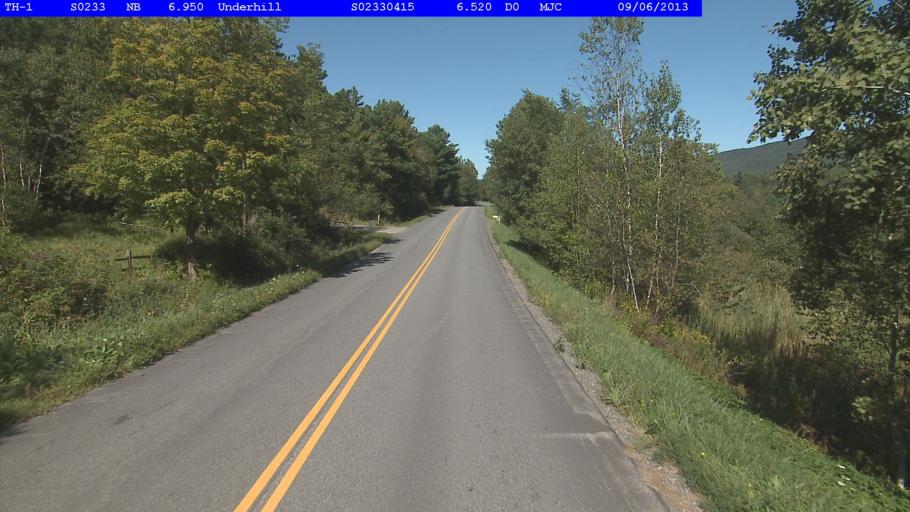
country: US
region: Vermont
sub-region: Chittenden County
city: Jericho
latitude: 44.5589
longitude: -72.8669
